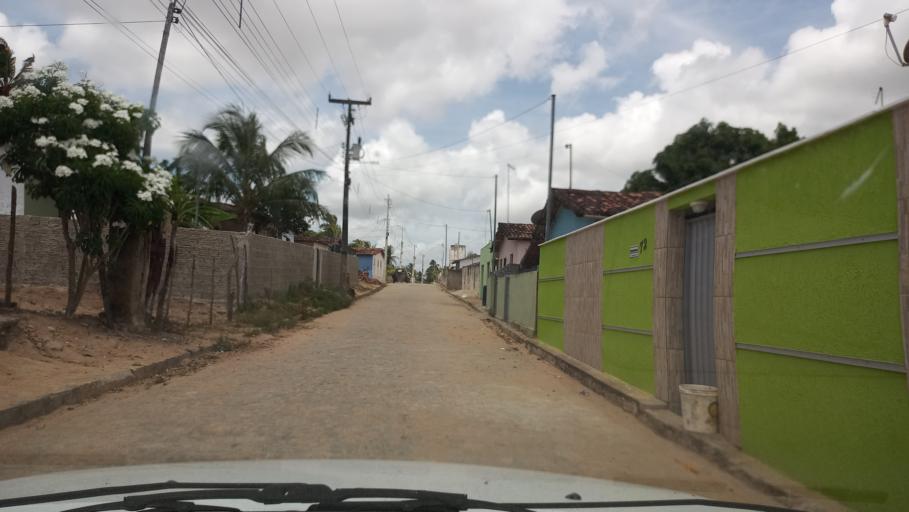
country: BR
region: Rio Grande do Norte
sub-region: Goianinha
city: Goianinha
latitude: -6.2879
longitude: -35.2827
